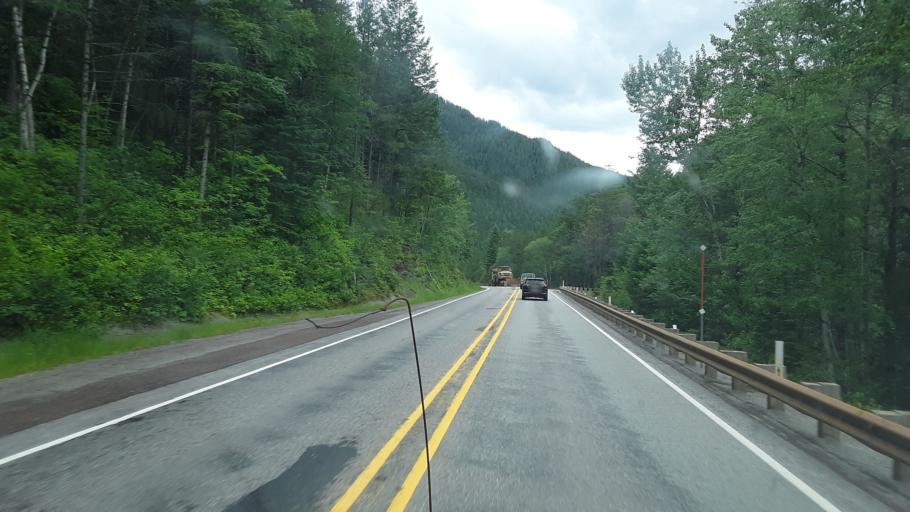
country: US
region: Montana
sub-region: Flathead County
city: Columbia Falls
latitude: 48.4936
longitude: -113.8992
